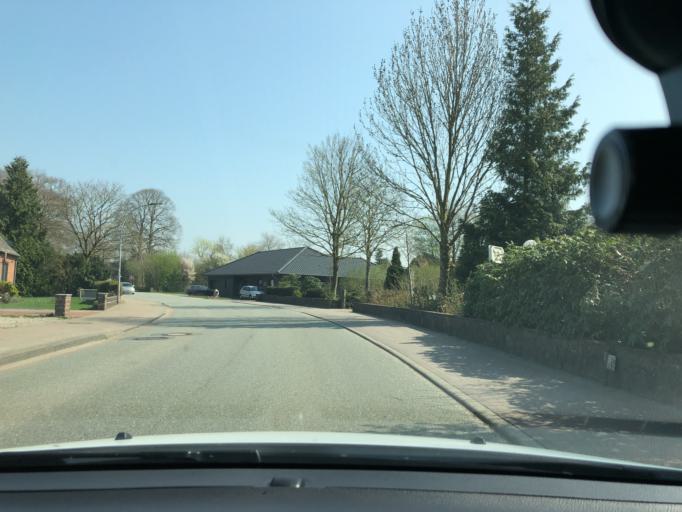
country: DE
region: Schleswig-Holstein
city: Wanderup
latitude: 54.6881
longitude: 9.3335
